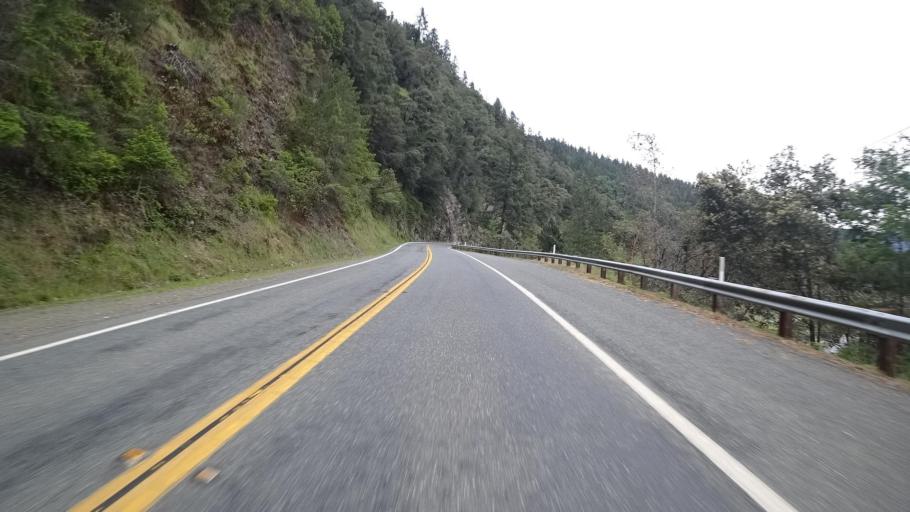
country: US
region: California
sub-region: Humboldt County
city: Willow Creek
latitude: 40.9894
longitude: -123.6369
